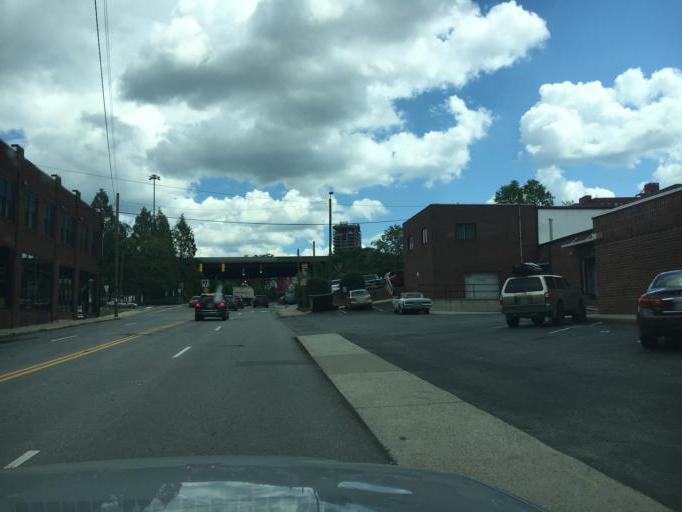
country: US
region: North Carolina
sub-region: Buncombe County
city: Asheville
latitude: 35.6004
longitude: -82.5551
